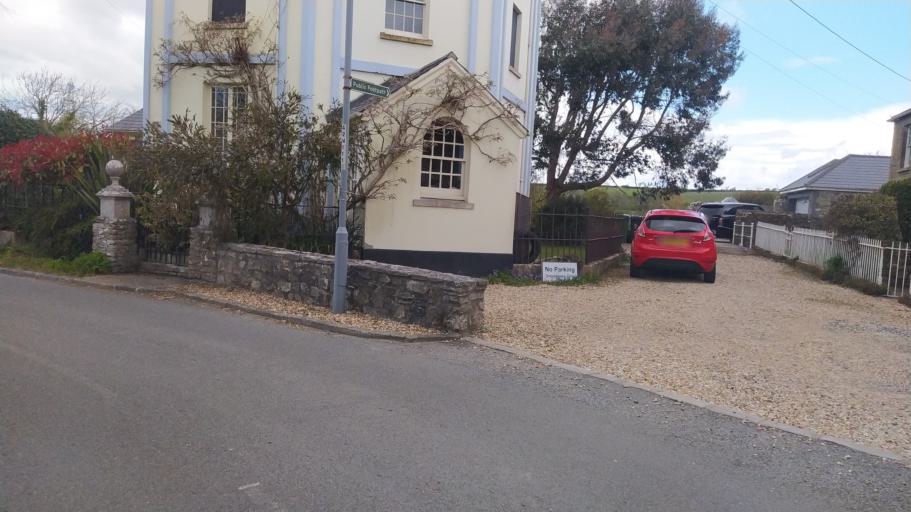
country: GB
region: England
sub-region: Dorset
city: Chickerell
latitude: 50.6431
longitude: -2.4775
